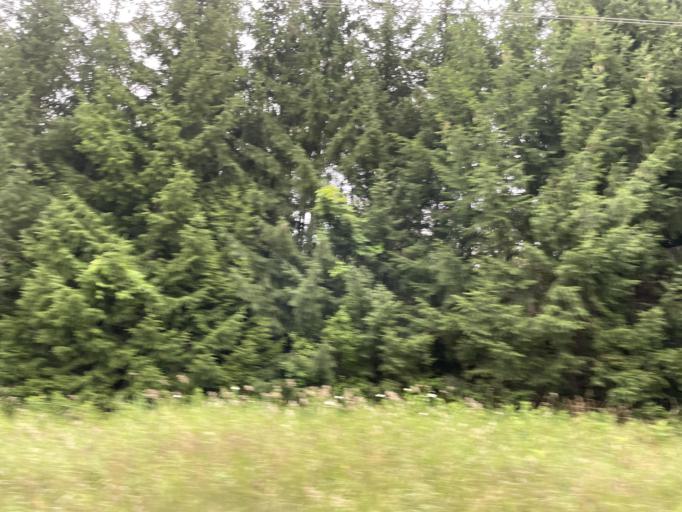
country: CA
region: Ontario
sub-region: Wellington County
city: Guelph
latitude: 43.5926
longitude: -80.2751
